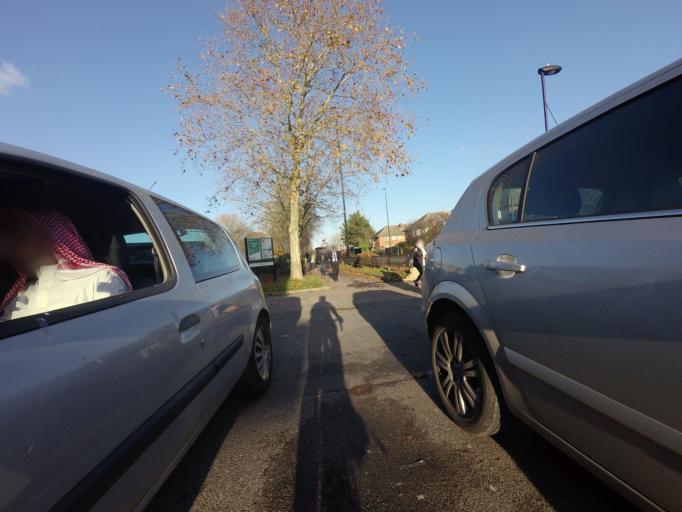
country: GB
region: England
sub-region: Greater London
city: Feltham
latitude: 51.4505
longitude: -0.4070
